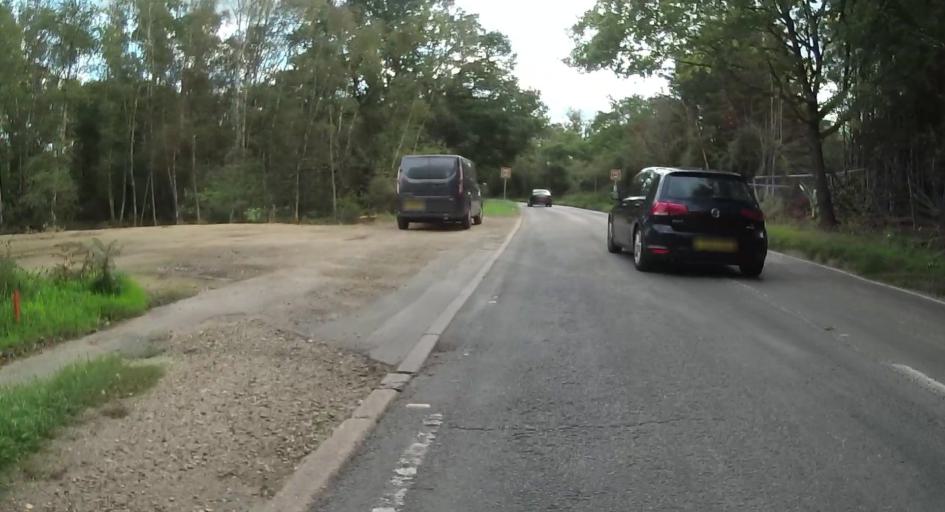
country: GB
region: England
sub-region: Surrey
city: Chobham
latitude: 51.3628
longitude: -0.6094
